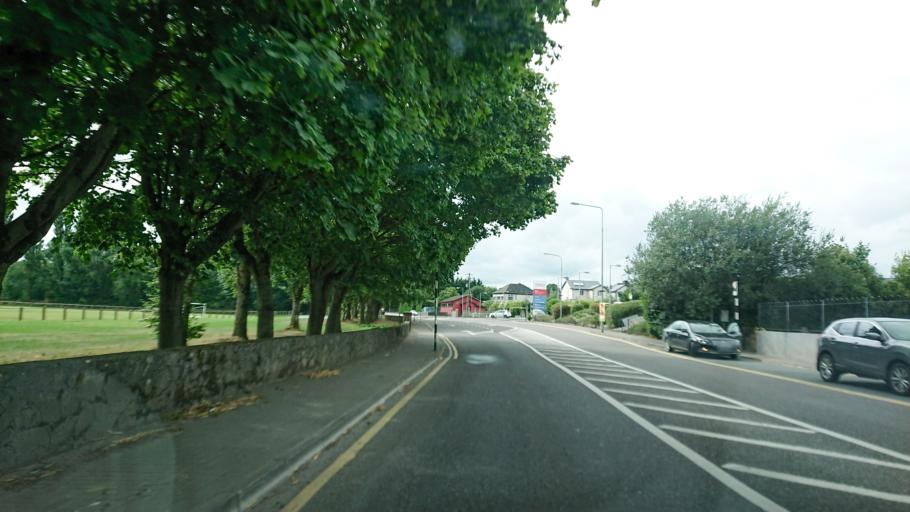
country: IE
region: Munster
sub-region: County Cork
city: Mallow
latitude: 52.1355
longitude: -8.6459
